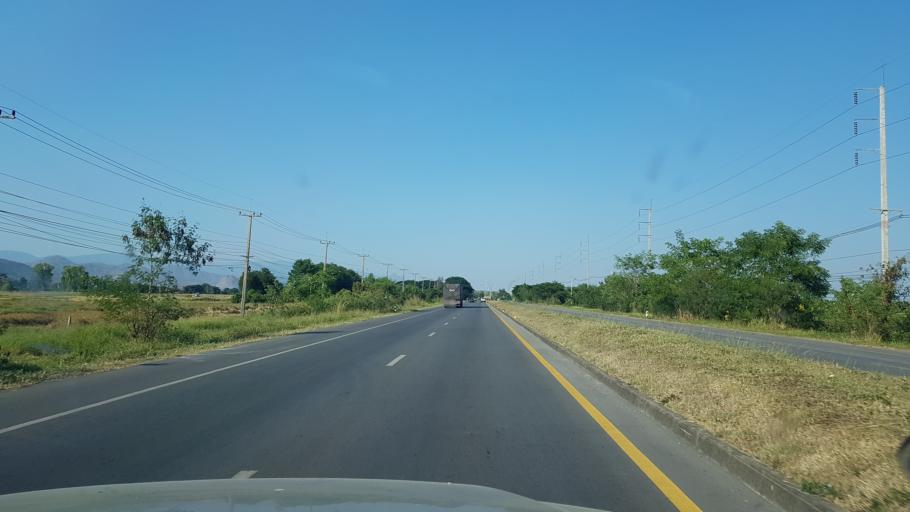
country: TH
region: Phetchabun
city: Khao Kho
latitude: 16.6173
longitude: 101.1597
